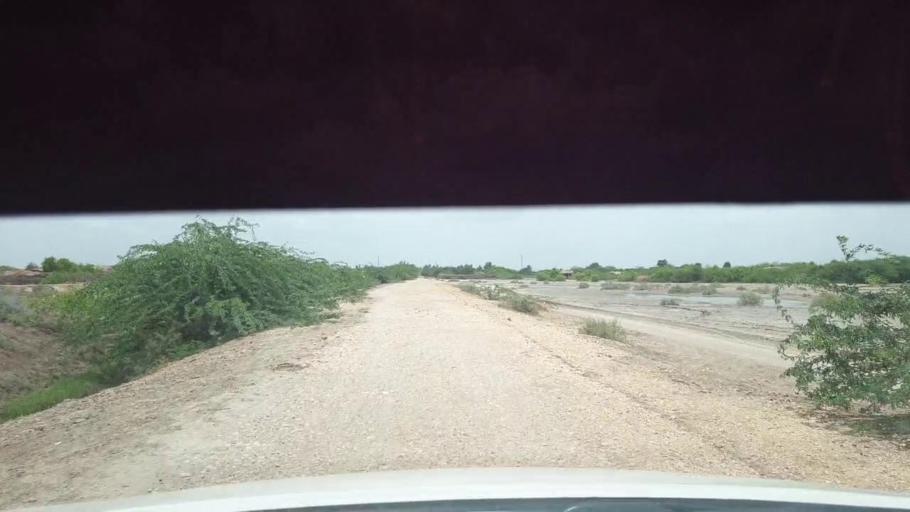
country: PK
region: Sindh
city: Kadhan
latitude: 24.4867
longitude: 69.0027
